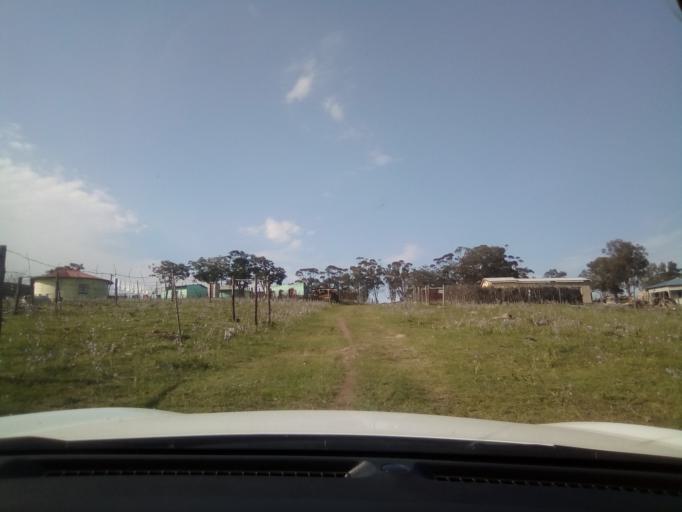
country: ZA
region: Eastern Cape
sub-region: Buffalo City Metropolitan Municipality
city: Bhisho
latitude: -32.9836
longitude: 27.2572
